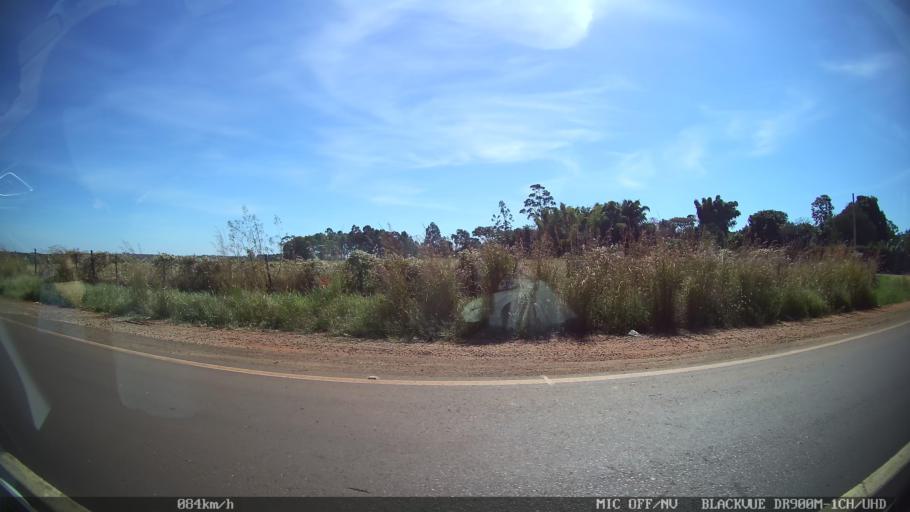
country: BR
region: Sao Paulo
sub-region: Franca
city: Franca
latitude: -20.5565
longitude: -47.4979
